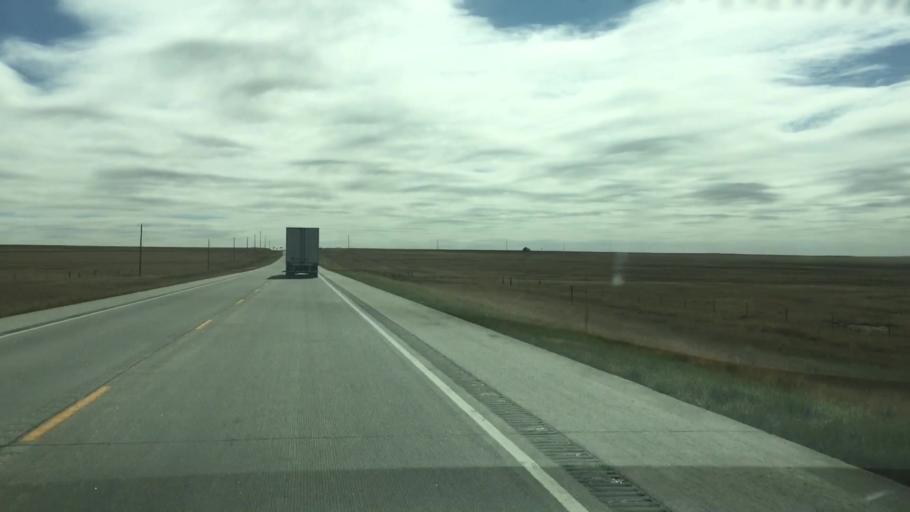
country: US
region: Colorado
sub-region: Lincoln County
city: Hugo
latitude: 38.9955
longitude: -103.2798
